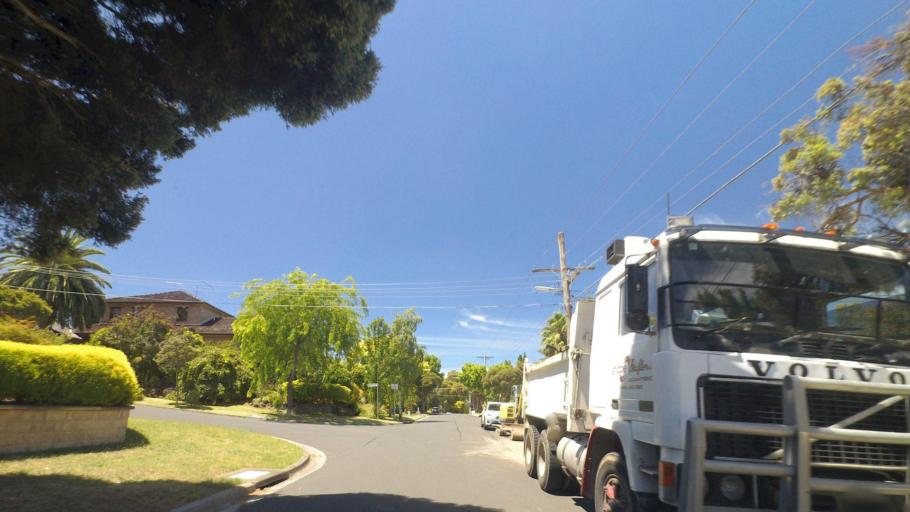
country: AU
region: Victoria
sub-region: Maroondah
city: Croydon North
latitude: -37.7726
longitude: 145.3158
